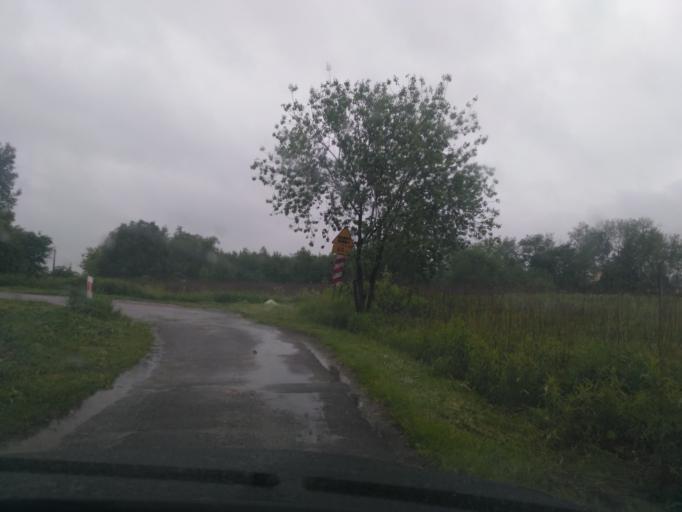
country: PL
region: Subcarpathian Voivodeship
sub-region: Powiat jasielski
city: Jaslo
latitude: 49.7467
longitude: 21.5111
